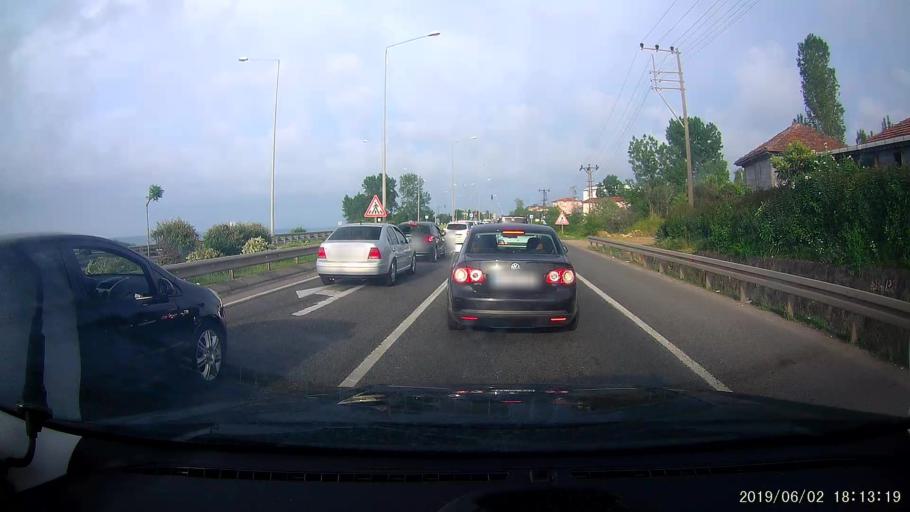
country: TR
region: Ordu
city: Unieh
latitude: 41.1066
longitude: 37.3677
